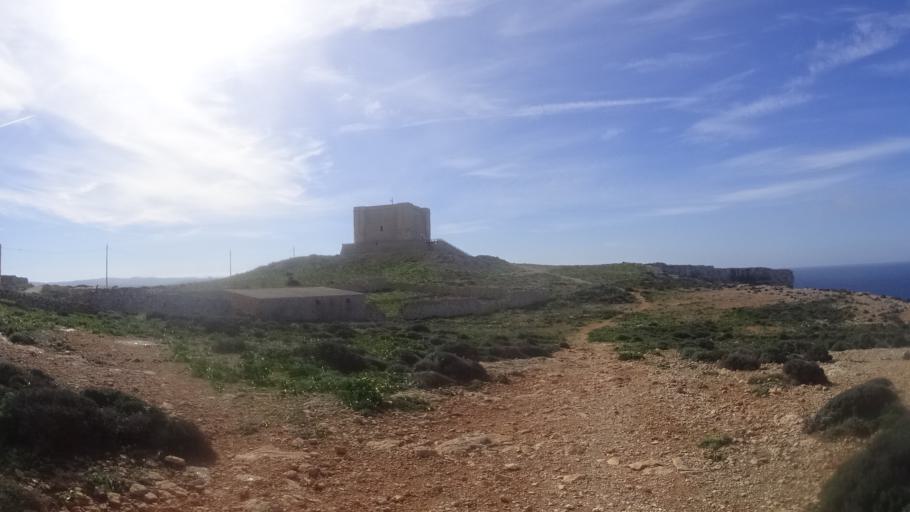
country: MT
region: Il-Qala
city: Qala
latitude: 36.0085
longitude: 14.3299
